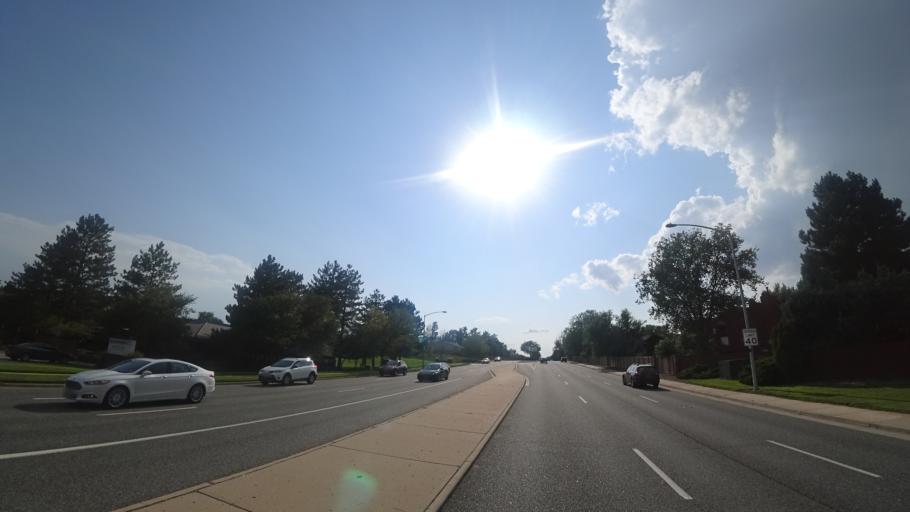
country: US
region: Colorado
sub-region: Arapahoe County
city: Dove Valley
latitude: 39.6386
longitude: -104.7993
